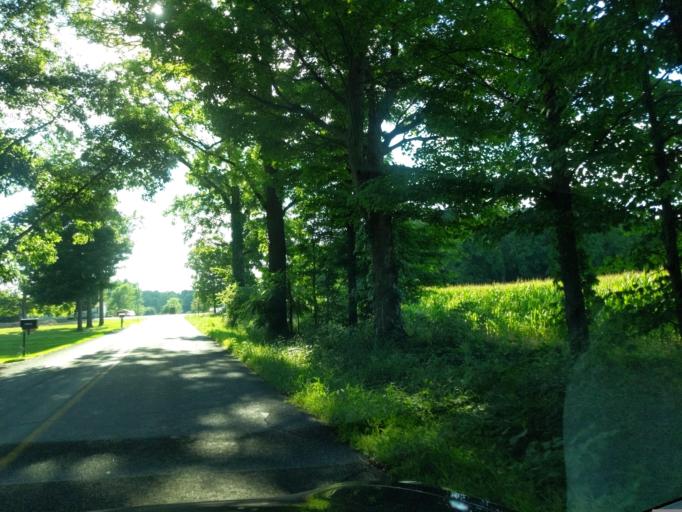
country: US
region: Michigan
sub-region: Ingham County
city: Mason
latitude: 42.5746
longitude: -84.4818
